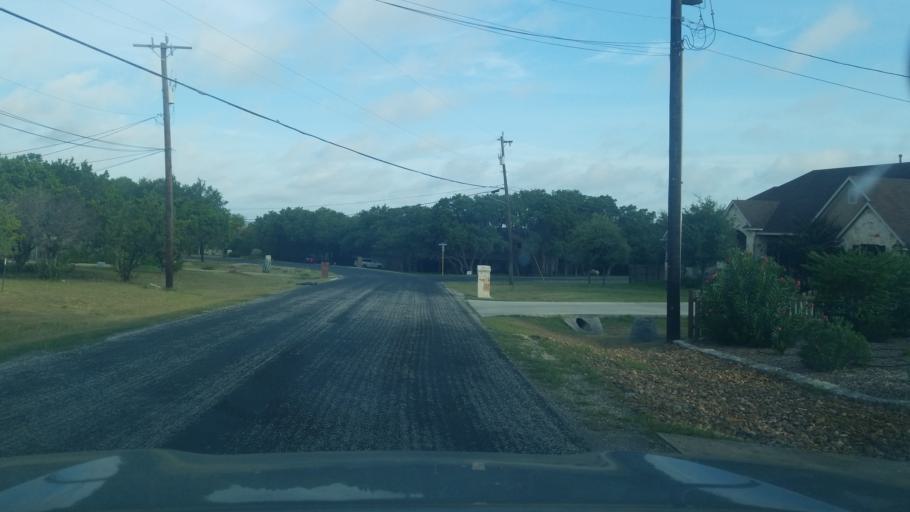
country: US
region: Texas
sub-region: Bexar County
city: Timberwood Park
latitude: 29.7016
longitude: -98.5013
